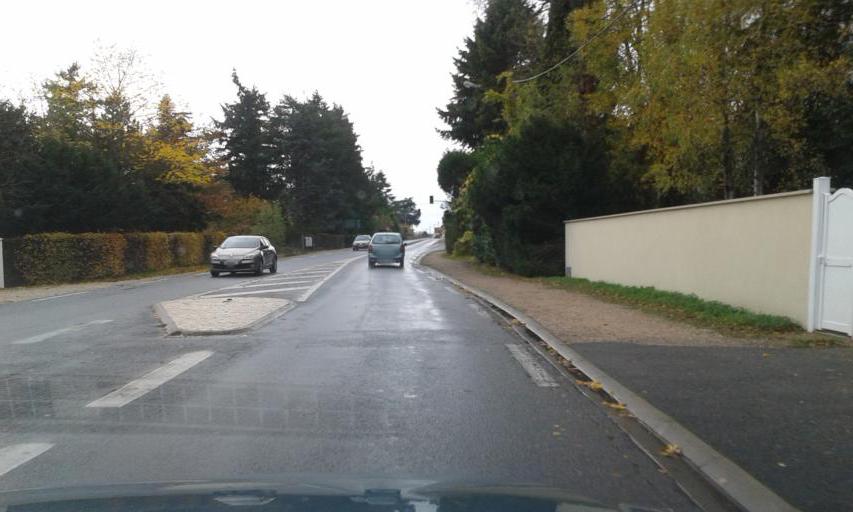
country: FR
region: Centre
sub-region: Departement du Loiret
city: Mareau-aux-Pres
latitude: 47.8648
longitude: 1.7688
